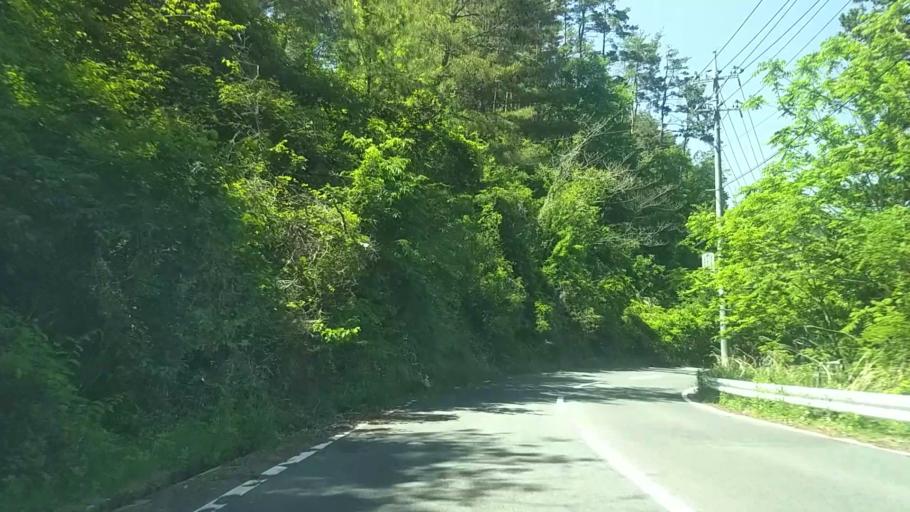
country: JP
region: Yamanashi
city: Nirasaki
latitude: 35.8525
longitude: 138.4327
